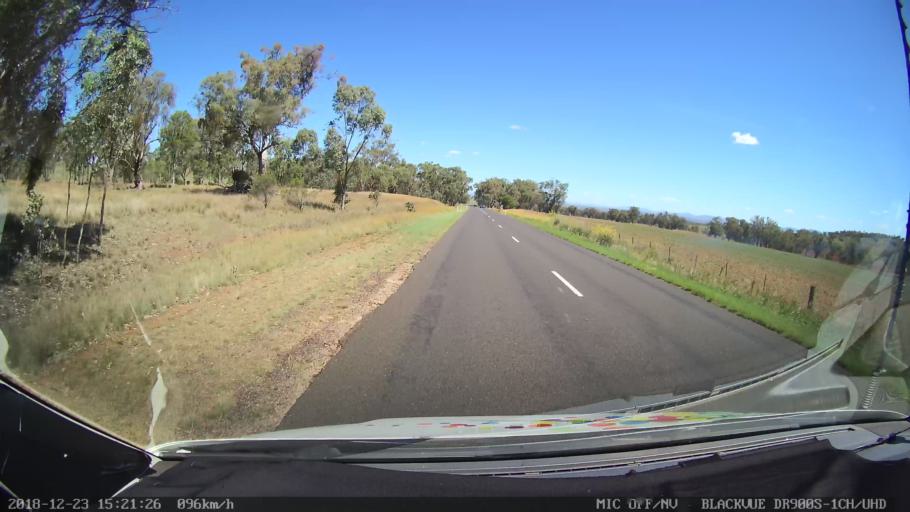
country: AU
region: New South Wales
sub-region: Tamworth Municipality
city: Manilla
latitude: -30.8564
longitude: 150.7966
